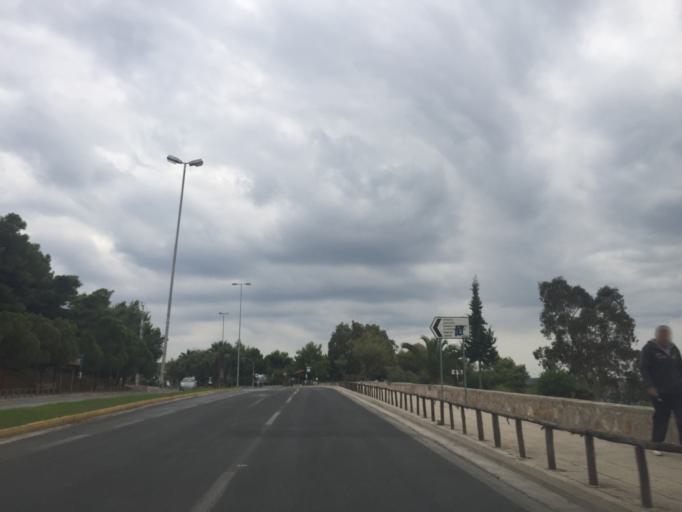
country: GR
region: Attica
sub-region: Nomarchia Anatolikis Attikis
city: Vouliagmeni
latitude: 37.8107
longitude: 23.7822
